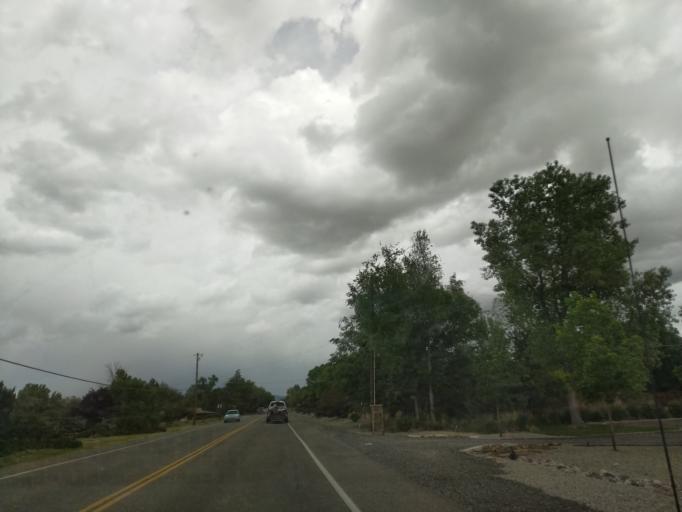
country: US
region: Colorado
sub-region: Mesa County
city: Grand Junction
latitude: 39.1004
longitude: -108.5616
